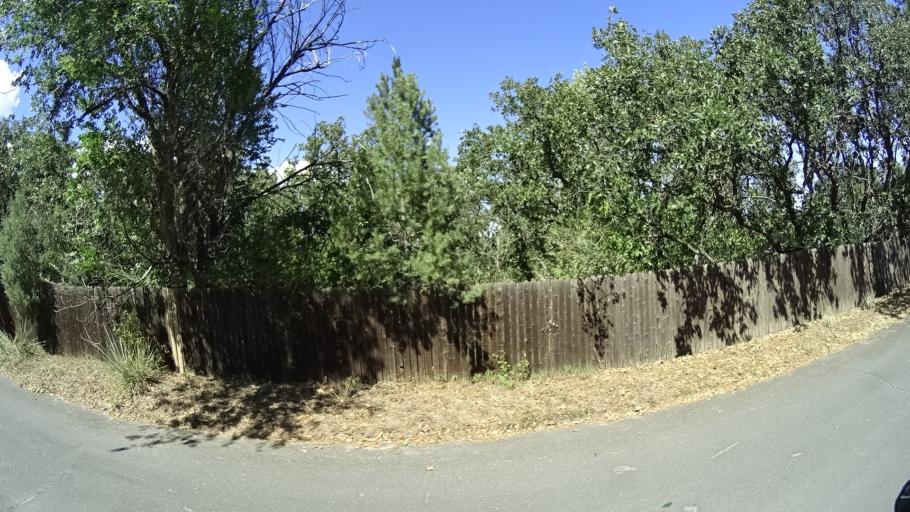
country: US
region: Colorado
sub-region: El Paso County
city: Colorado Springs
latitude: 38.7845
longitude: -104.8602
